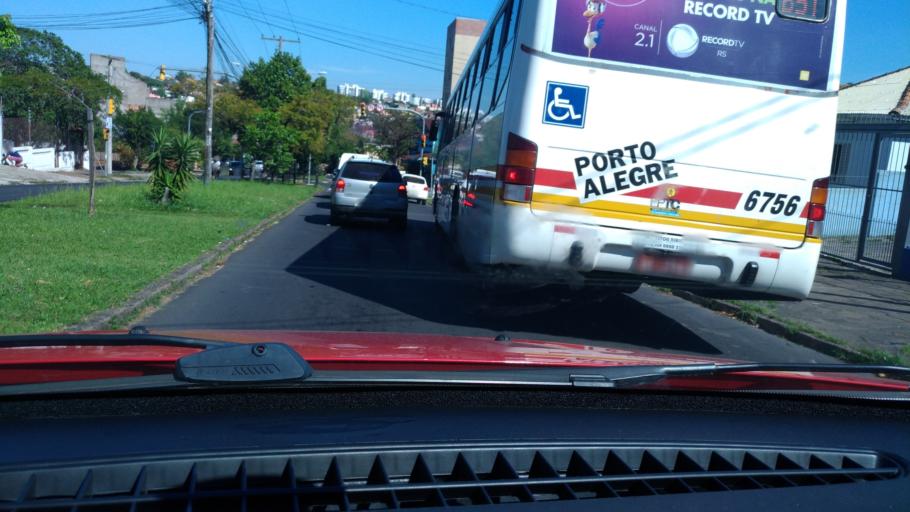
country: BR
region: Rio Grande do Sul
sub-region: Porto Alegre
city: Porto Alegre
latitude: -30.0302
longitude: -51.1397
